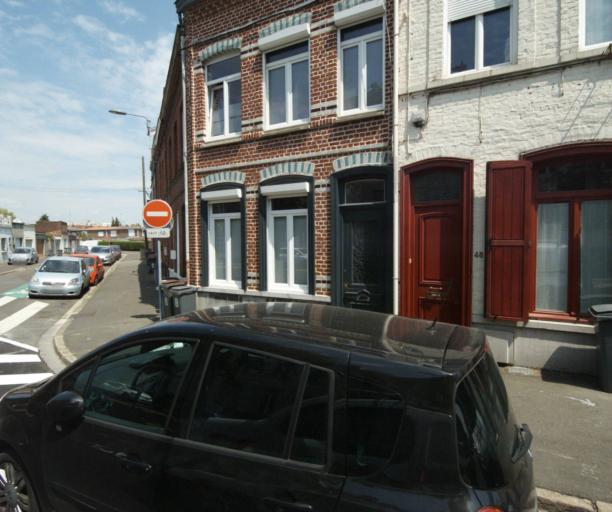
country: FR
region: Nord-Pas-de-Calais
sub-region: Departement du Nord
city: Saint-Andre-lez-Lille
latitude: 50.6548
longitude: 3.0525
